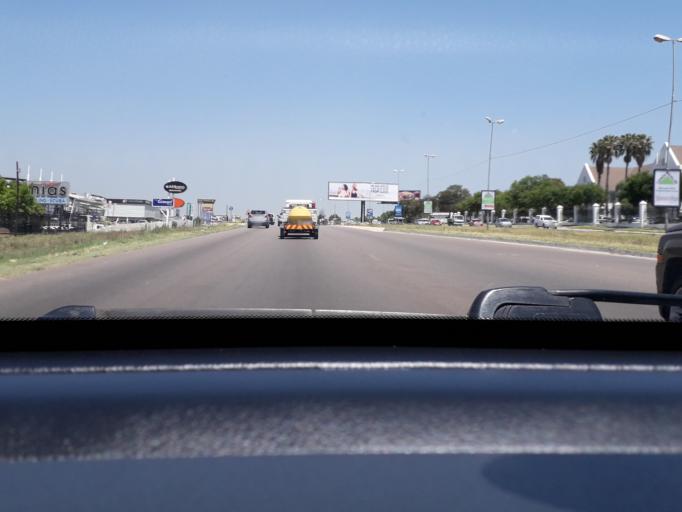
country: ZA
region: Gauteng
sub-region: City of Johannesburg Metropolitan Municipality
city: Midrand
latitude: -26.0530
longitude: 28.0905
